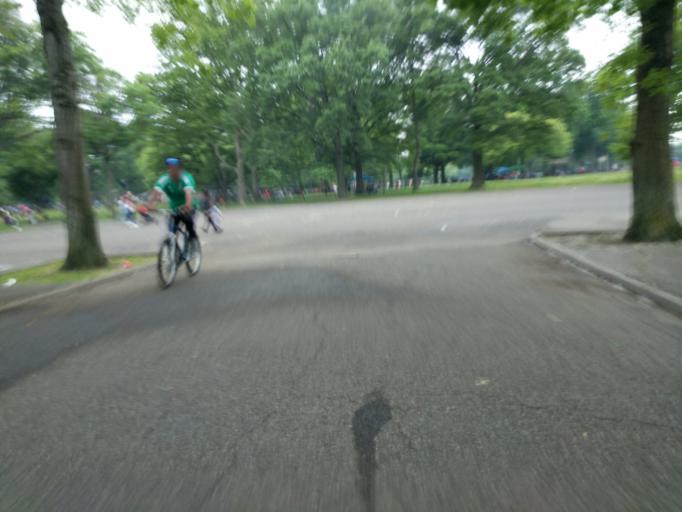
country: US
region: New York
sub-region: Queens County
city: Jamaica
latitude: 40.7464
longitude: -73.8385
